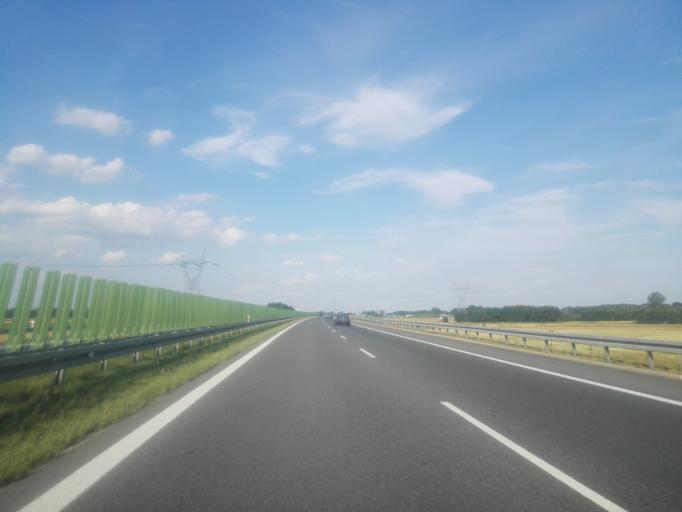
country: PL
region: Lower Silesian Voivodeship
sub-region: Powiat wroclawski
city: Dlugoleka
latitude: 51.2208
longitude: 17.1478
